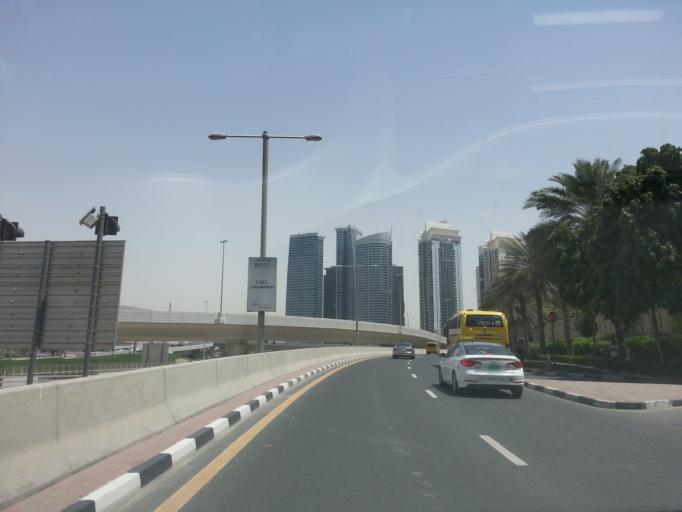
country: AE
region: Dubai
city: Dubai
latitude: 25.0867
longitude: 55.1498
